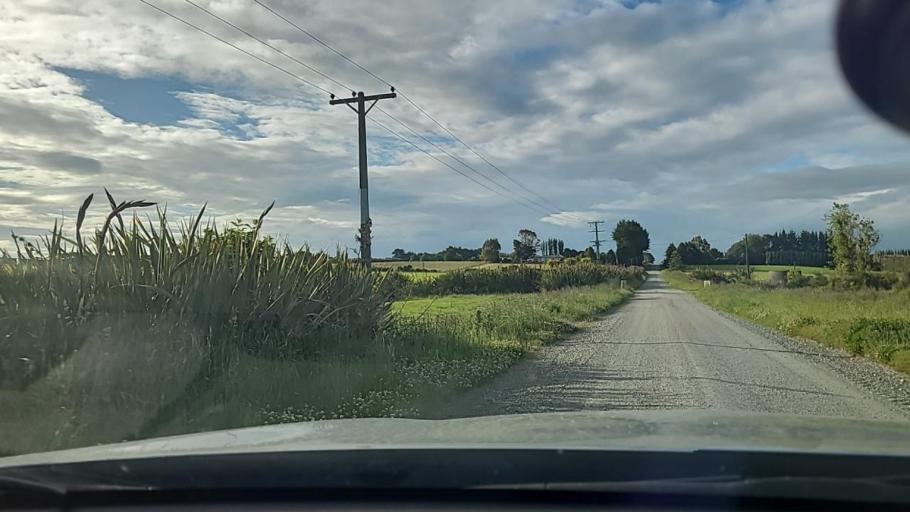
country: NZ
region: Southland
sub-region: Invercargill City
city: Invercargill
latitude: -46.3630
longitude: 168.5962
